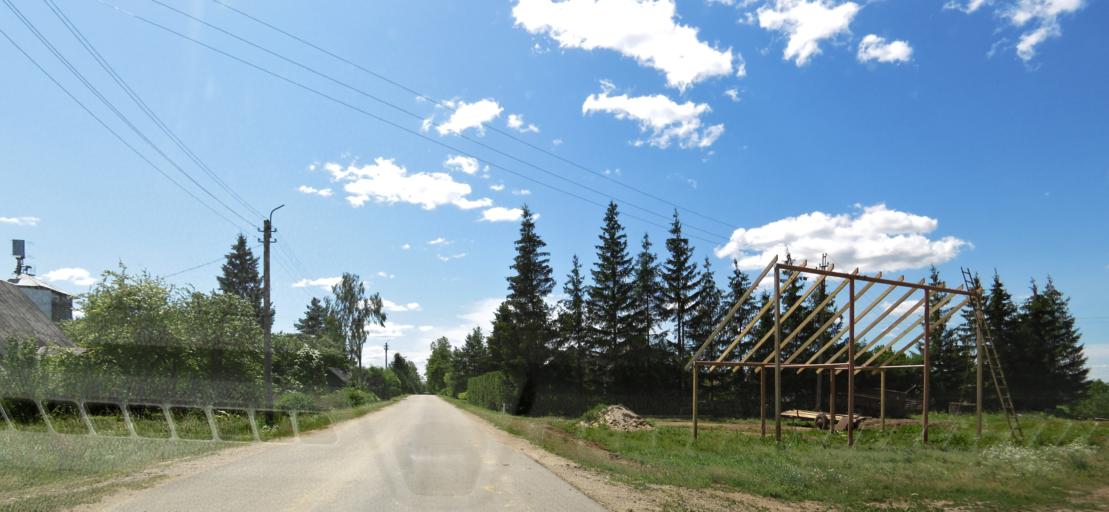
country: LT
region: Panevezys
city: Pasvalys
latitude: 56.2324
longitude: 24.4131
